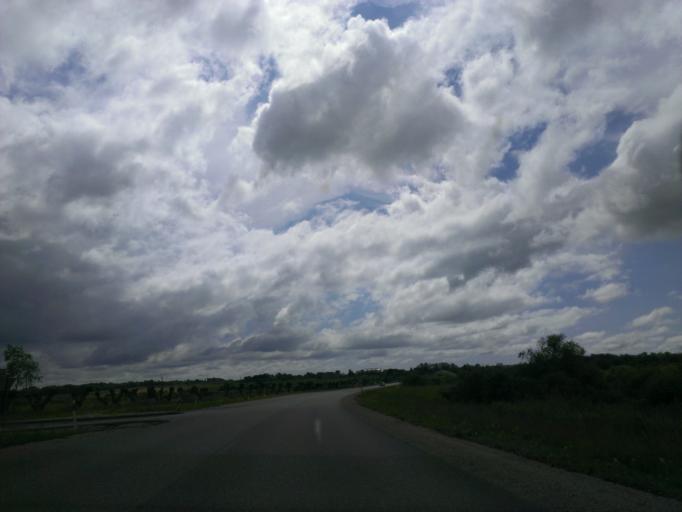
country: LV
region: Durbe
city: Liegi
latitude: 56.5878
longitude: 21.3585
